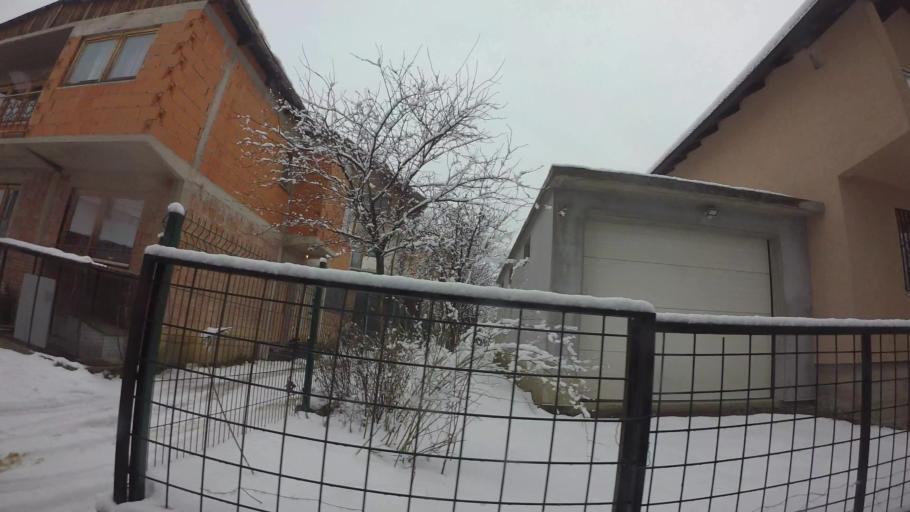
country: BA
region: Federation of Bosnia and Herzegovina
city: Vogosca
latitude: 43.8750
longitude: 18.3226
